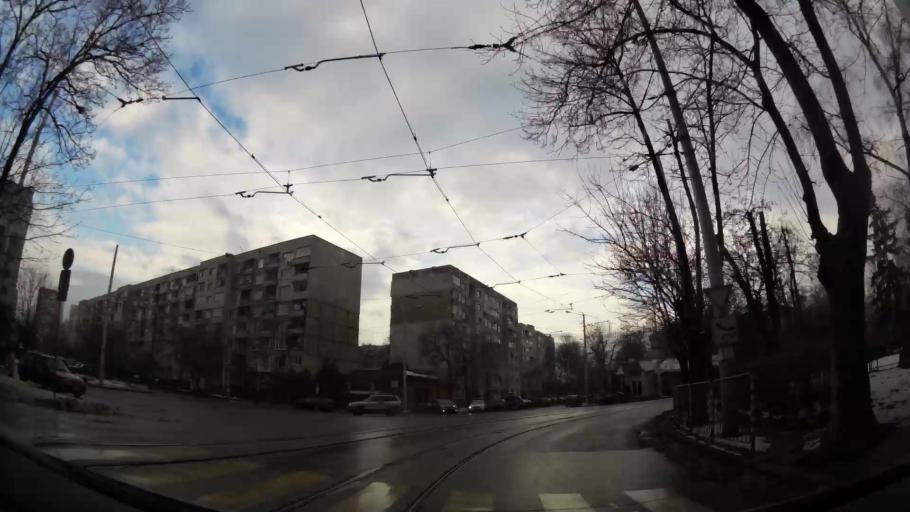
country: BG
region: Sofia-Capital
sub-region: Stolichna Obshtina
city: Sofia
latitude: 42.7089
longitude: 23.2877
